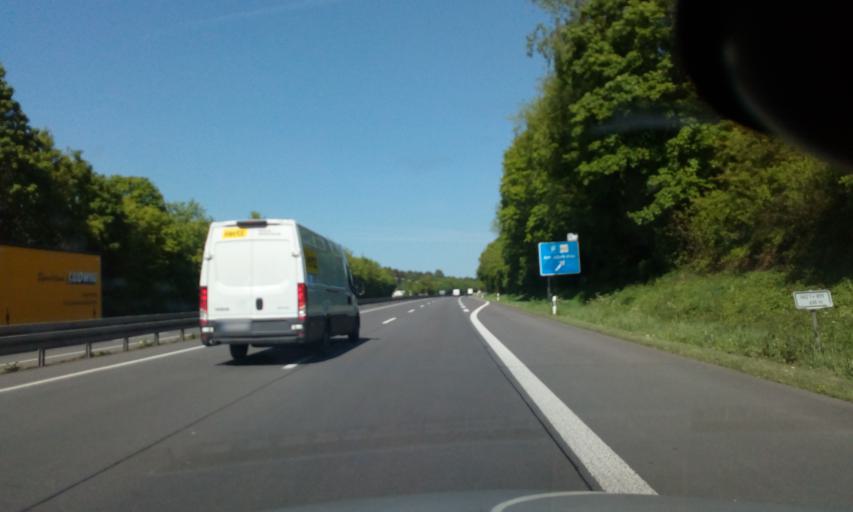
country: DE
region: North Rhine-Westphalia
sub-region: Regierungsbezirk Koln
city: Weilerswist
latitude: 50.7837
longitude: 6.8399
